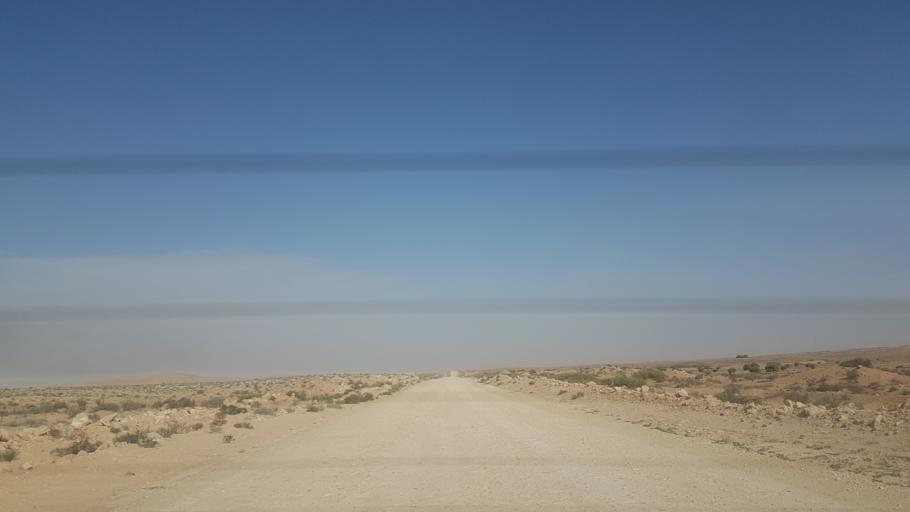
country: TN
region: Qabis
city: El Hamma
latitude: 33.6646
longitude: 9.7355
